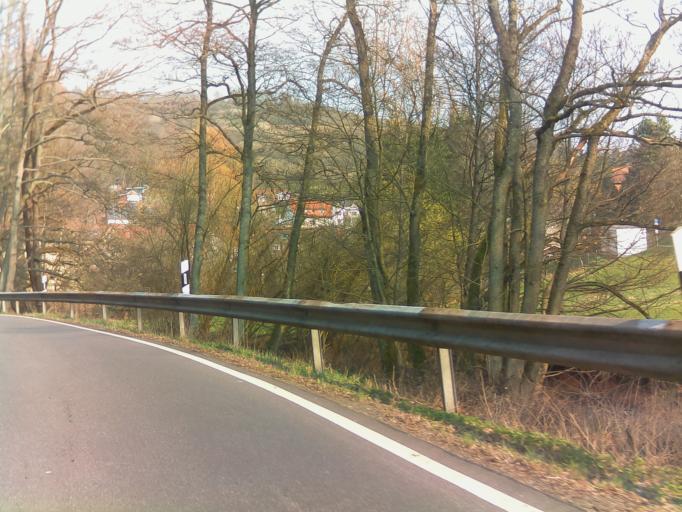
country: DE
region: Rheinland-Pfalz
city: Fockelberg
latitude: 49.5435
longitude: 7.4924
